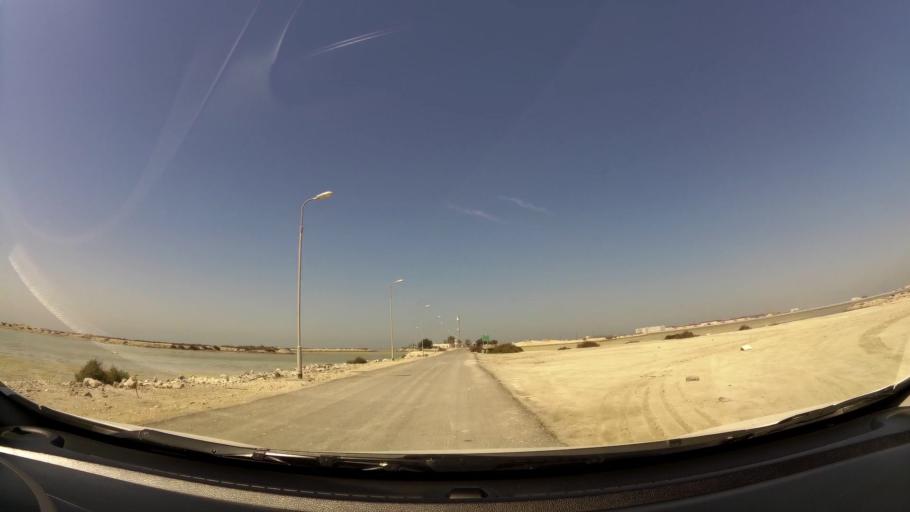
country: BH
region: Muharraq
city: Al Muharraq
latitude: 26.2893
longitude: 50.6248
